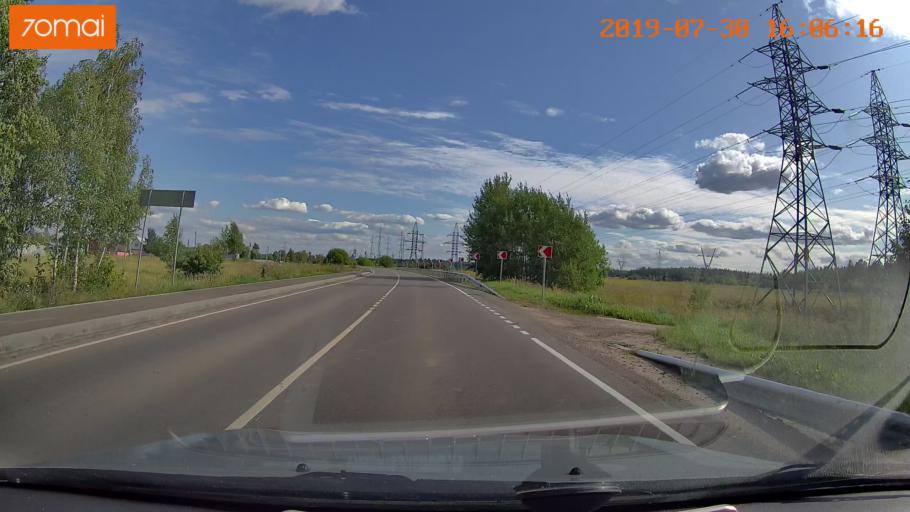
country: RU
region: Moskovskaya
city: Peski
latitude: 55.2575
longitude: 38.7158
